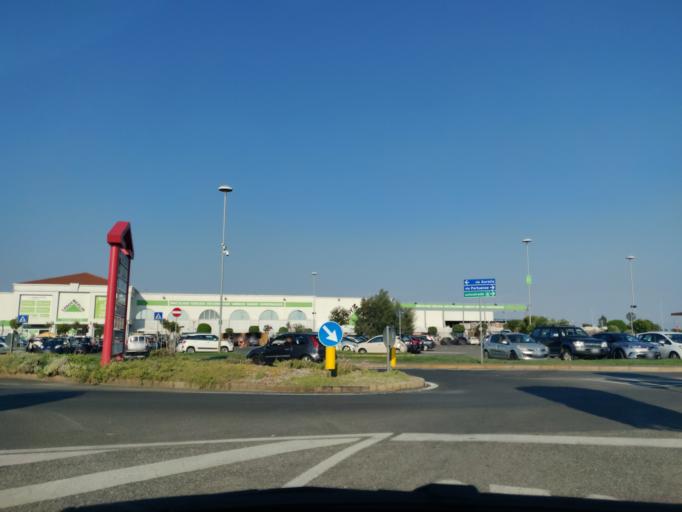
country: IT
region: Latium
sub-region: Citta metropolitana di Roma Capitale
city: Npp 23 (Parco Leonardo)
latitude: 41.8076
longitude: 12.3010
